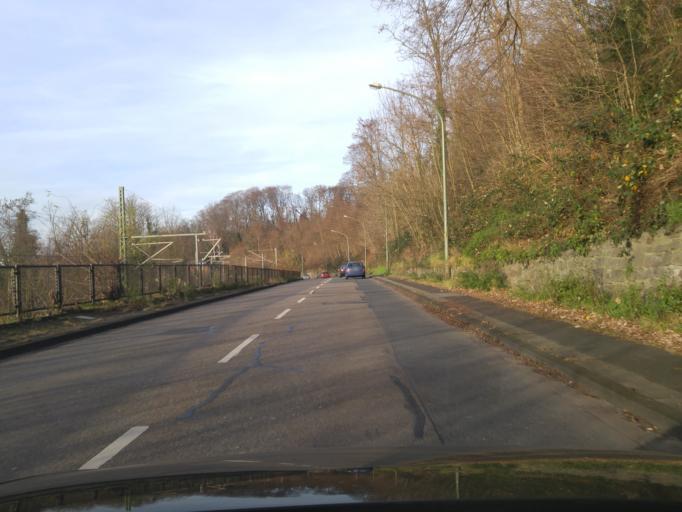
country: DE
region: North Rhine-Westphalia
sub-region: Regierungsbezirk Dusseldorf
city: Velbert
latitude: 51.4084
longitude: 7.0824
